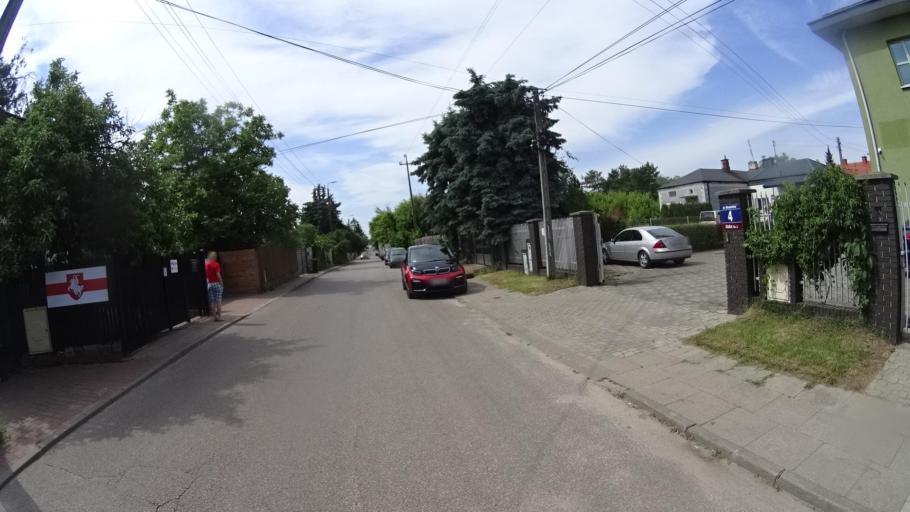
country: PL
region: Masovian Voivodeship
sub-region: Warszawa
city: Wlochy
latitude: 52.1788
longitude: 20.9301
